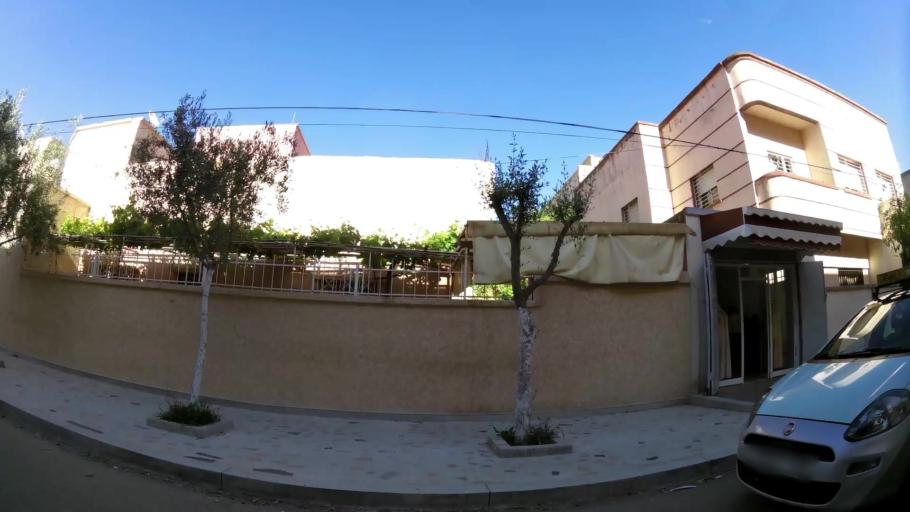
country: MA
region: Meknes-Tafilalet
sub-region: Meknes
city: Meknes
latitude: 33.8877
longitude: -5.5031
